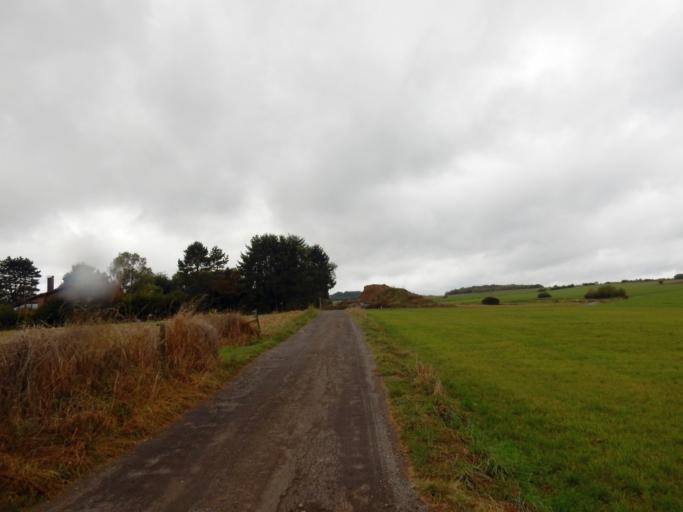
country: LU
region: Luxembourg
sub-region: Canton de Luxembourg
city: Olm
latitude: 49.6813
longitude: 6.0099
